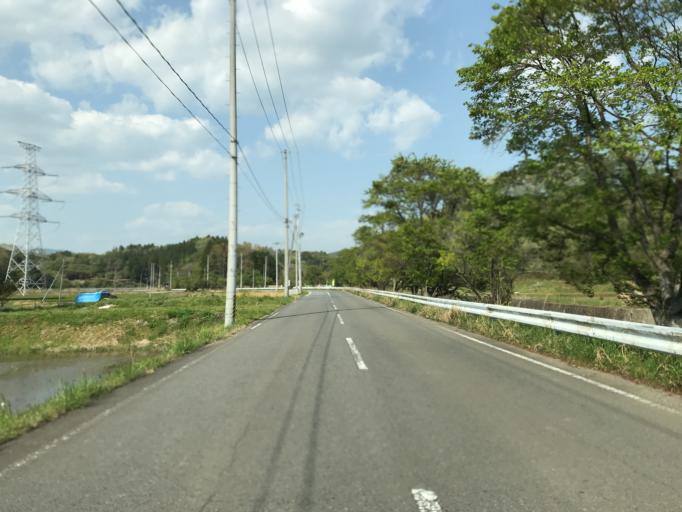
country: JP
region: Fukushima
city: Iwaki
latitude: 36.9643
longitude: 140.7558
